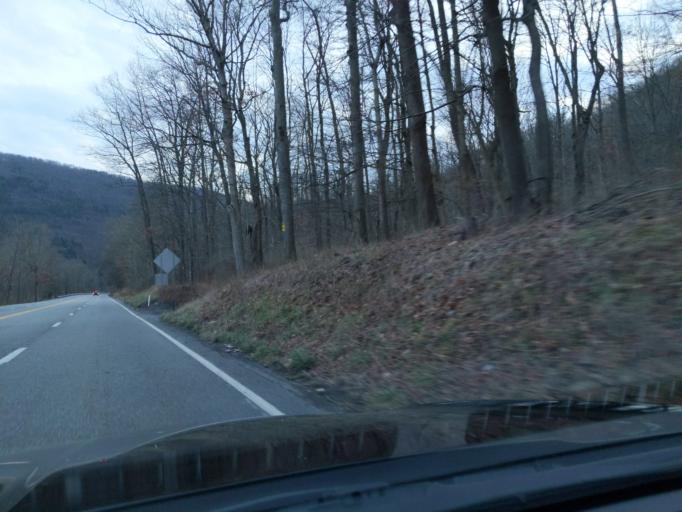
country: US
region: Pennsylvania
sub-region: Blair County
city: Williamsburg
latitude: 40.4935
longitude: -78.2453
